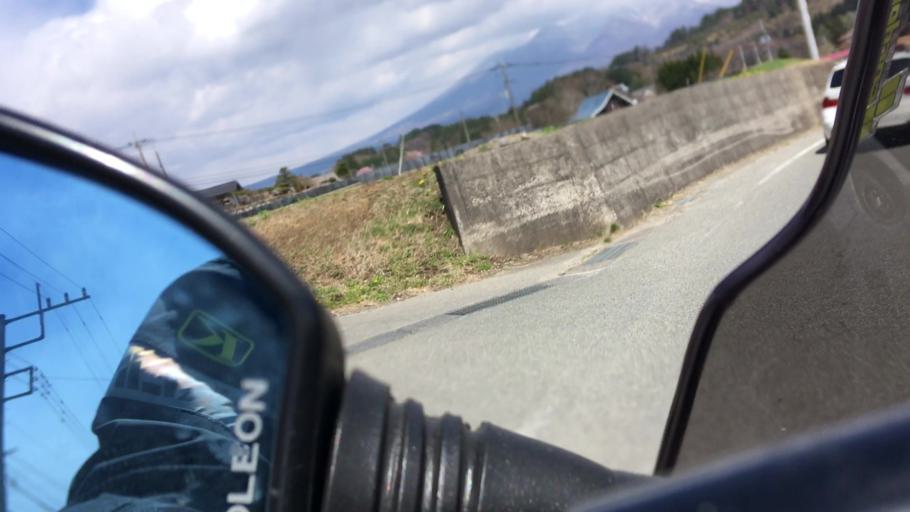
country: JP
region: Yamanashi
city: Nirasaki
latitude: 35.7874
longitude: 138.3214
